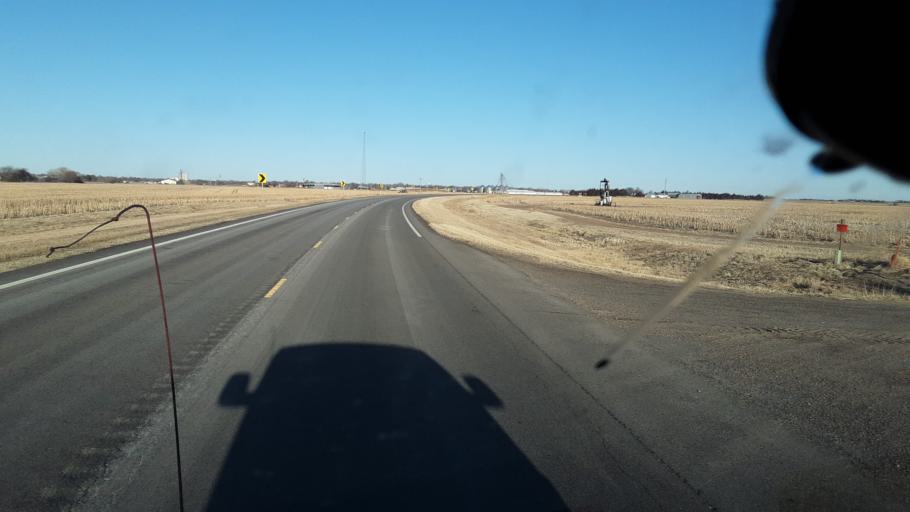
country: US
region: Kansas
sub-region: Barton County
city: Ellinwood
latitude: 38.3491
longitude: -98.5538
